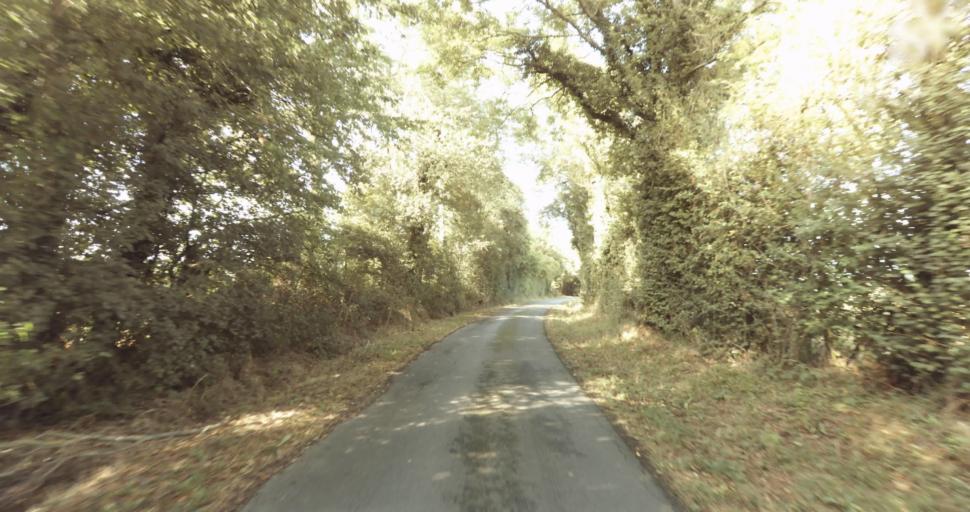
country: FR
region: Lower Normandy
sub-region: Departement de l'Orne
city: Vimoutiers
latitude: 48.9233
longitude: 0.1176
